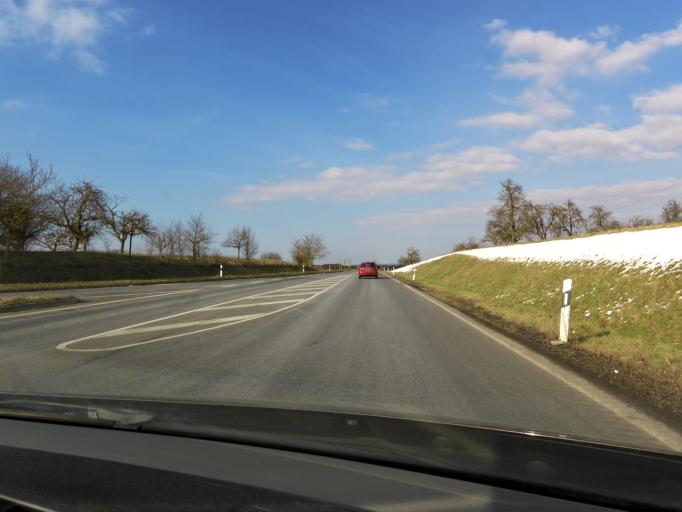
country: DE
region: Bavaria
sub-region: Regierungsbezirk Unterfranken
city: Geldersheim
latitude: 50.0162
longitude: 10.1256
